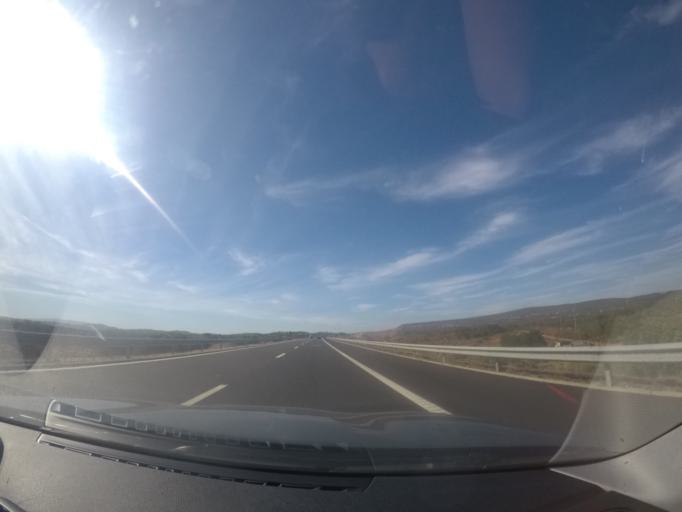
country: PT
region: Faro
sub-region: Silves
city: Sao Bartolomeu de Messines
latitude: 37.2133
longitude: -8.2393
